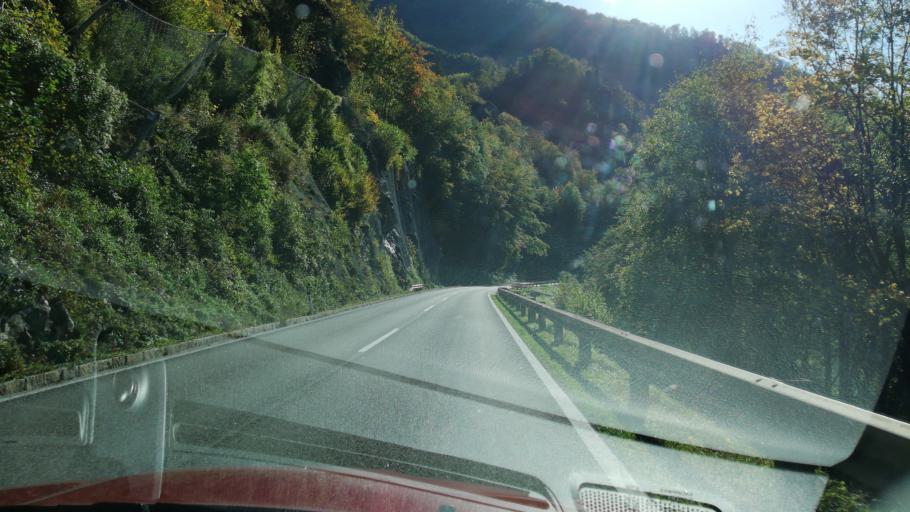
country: AT
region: Upper Austria
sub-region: Politischer Bezirk Steyr-Land
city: Weyer
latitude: 47.8722
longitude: 14.6071
